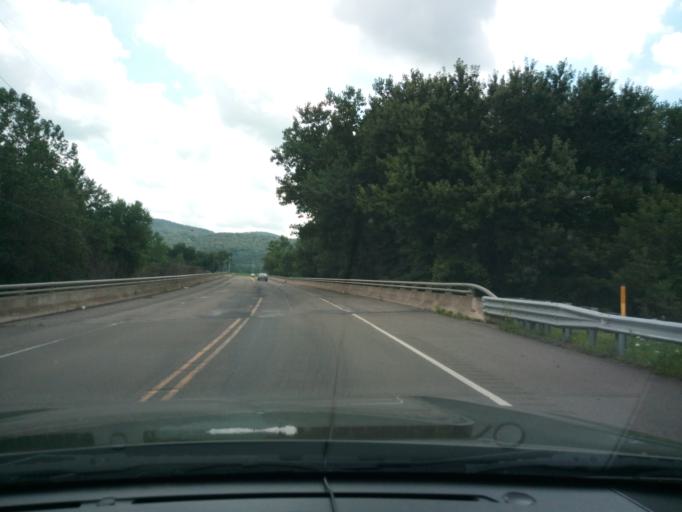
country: US
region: Pennsylvania
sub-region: Bradford County
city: South Waverly
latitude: 41.9877
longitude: -76.5531
